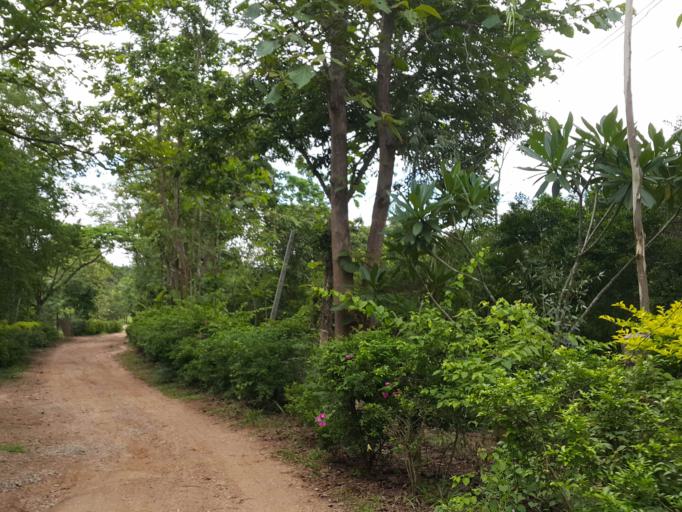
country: TH
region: Chiang Mai
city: San Sai
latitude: 18.9402
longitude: 98.9110
